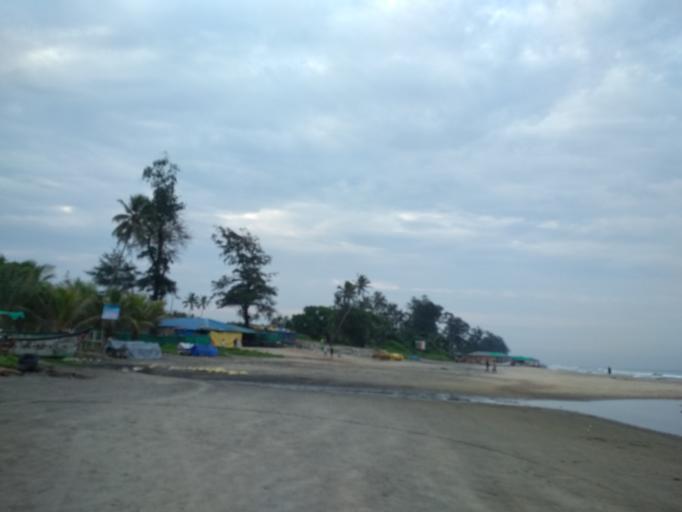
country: IN
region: Goa
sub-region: North Goa
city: Arambol
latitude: 15.6882
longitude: 73.7029
